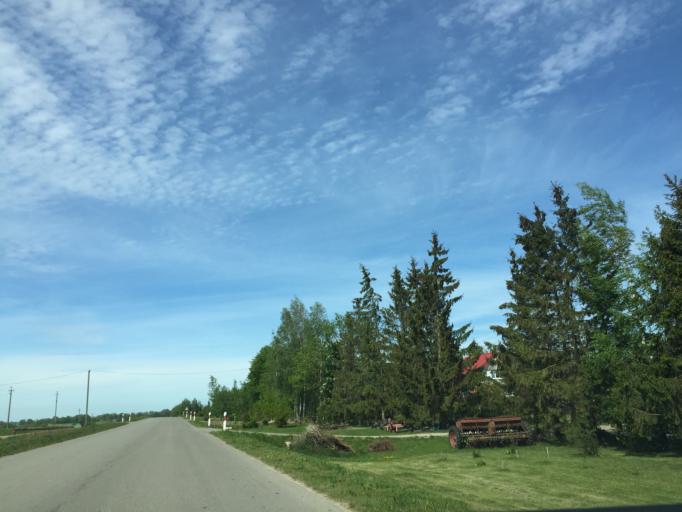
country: LT
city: Linkuva
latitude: 56.1073
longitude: 24.1668
